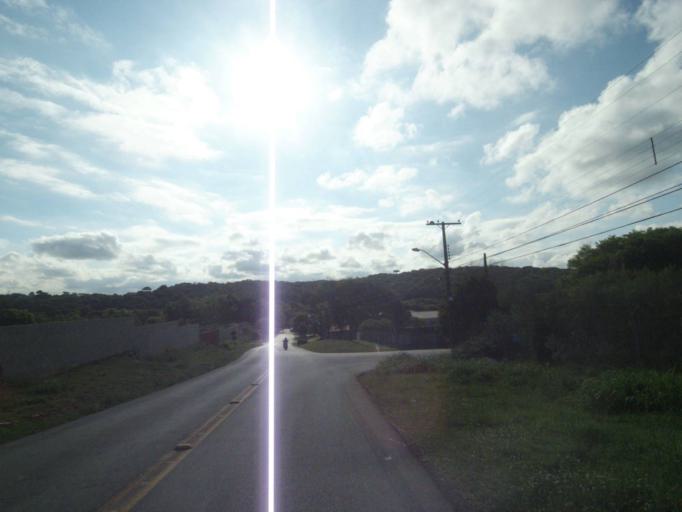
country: BR
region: Parana
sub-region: Curitiba
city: Curitiba
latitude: -25.3916
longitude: -49.3017
